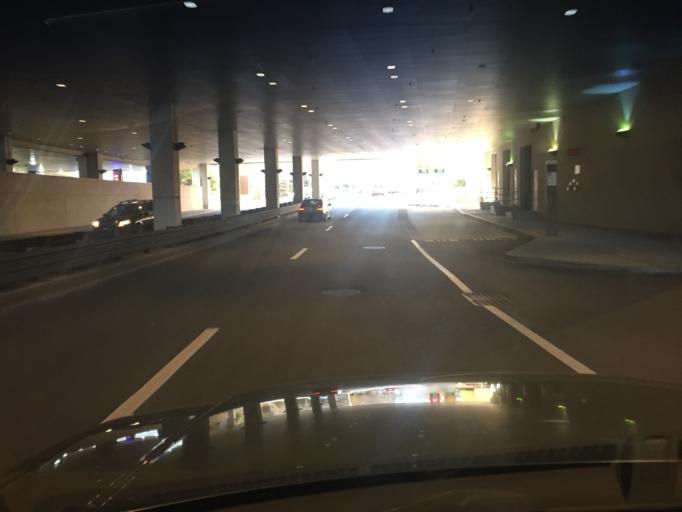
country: US
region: Massachusetts
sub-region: Middlesex County
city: Cochituate
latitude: 42.3020
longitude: -71.3833
